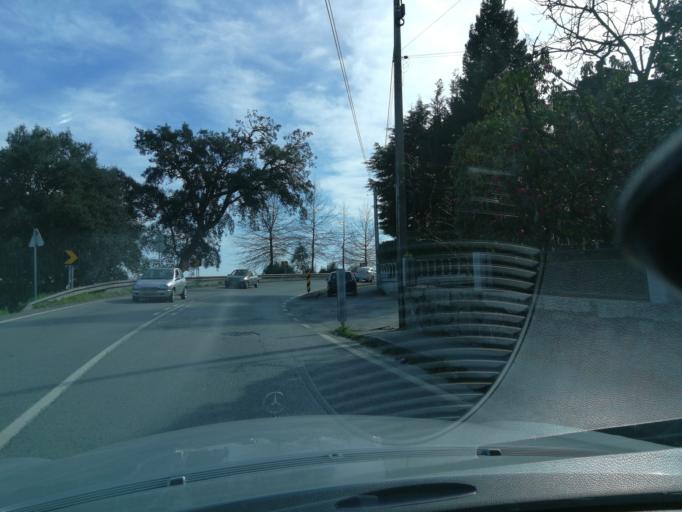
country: PT
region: Braga
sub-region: Vila Nova de Famalicao
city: Vila Nova de Famalicao
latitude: 41.4405
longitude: -8.4963
